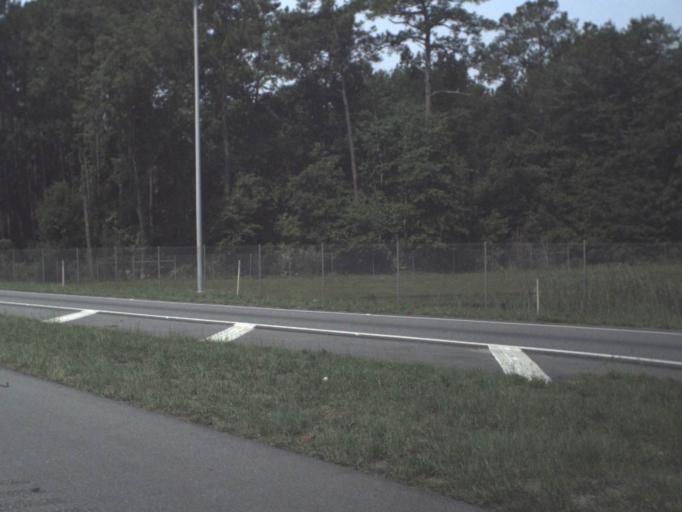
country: US
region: Georgia
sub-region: Camden County
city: Kingsland
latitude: 30.7241
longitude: -81.6650
